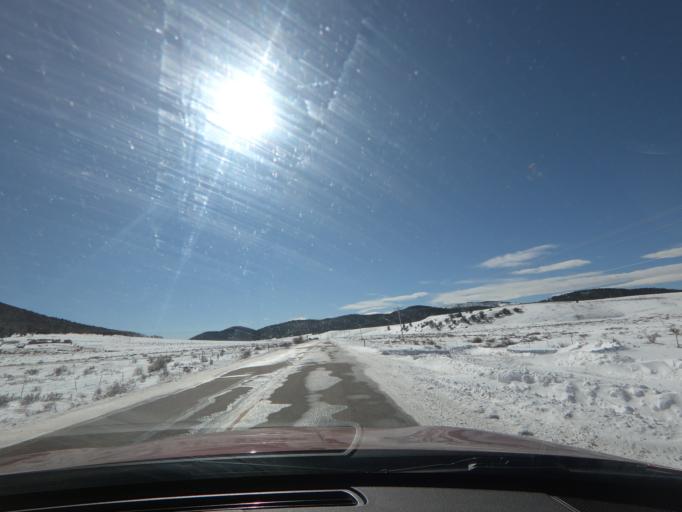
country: US
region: Colorado
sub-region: Teller County
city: Cripple Creek
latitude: 38.7785
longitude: -105.1215
